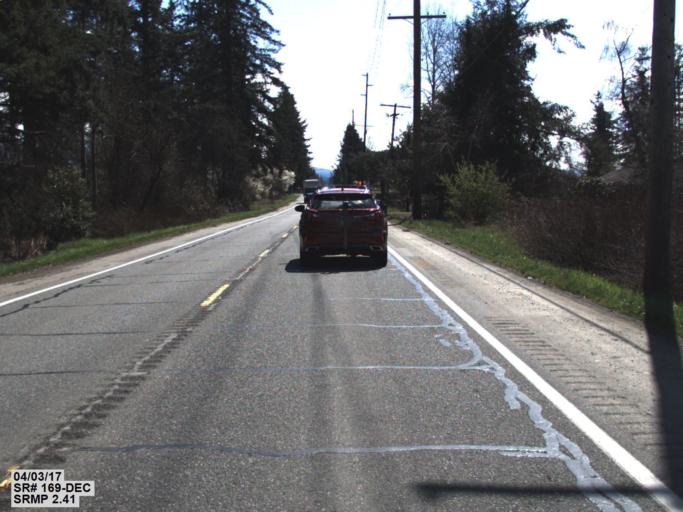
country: US
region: Washington
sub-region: King County
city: Enumclaw
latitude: 47.2390
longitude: -121.9897
